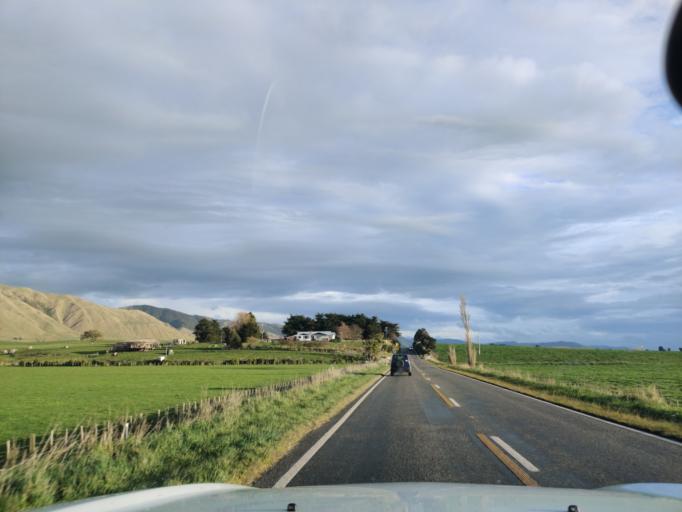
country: NZ
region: Manawatu-Wanganui
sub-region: Horowhenua District
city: Foxton
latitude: -40.5031
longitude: 175.4870
